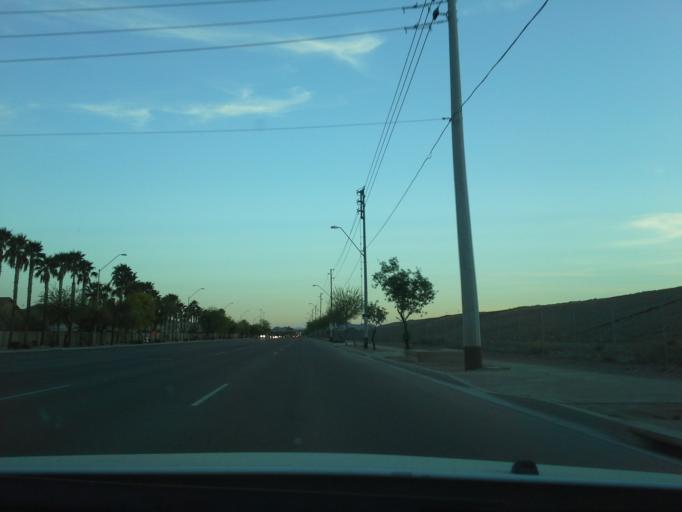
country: US
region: Arizona
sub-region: Maricopa County
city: Glendale
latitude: 33.6769
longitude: -112.0658
